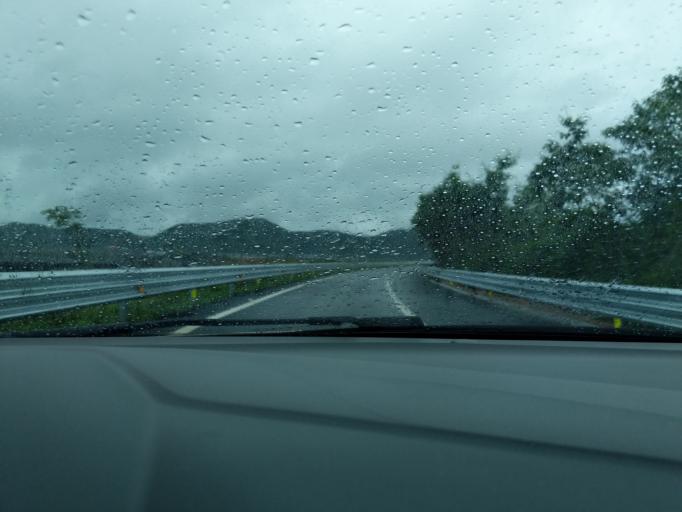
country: CN
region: Guangdong
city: Pingshi
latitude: 22.2413
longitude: 112.3036
